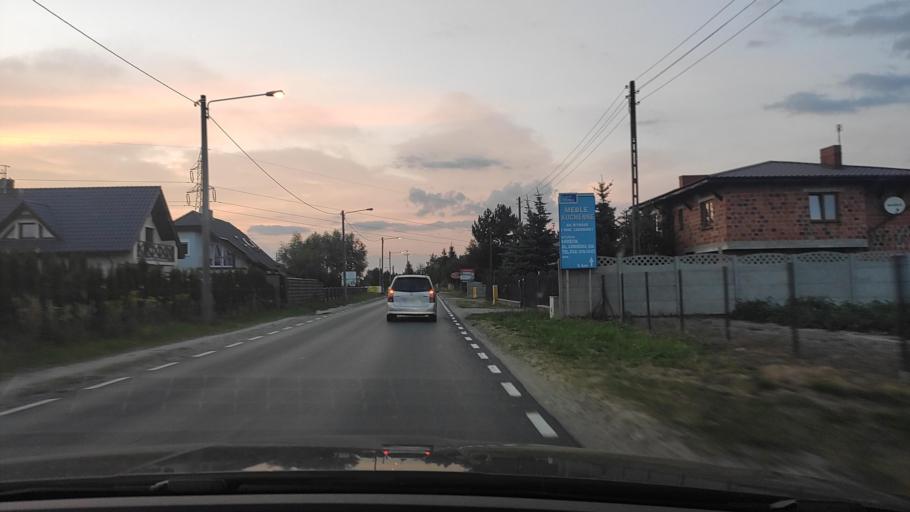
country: PL
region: Greater Poland Voivodeship
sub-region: Powiat poznanski
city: Swarzedz
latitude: 52.3901
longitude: 17.0929
